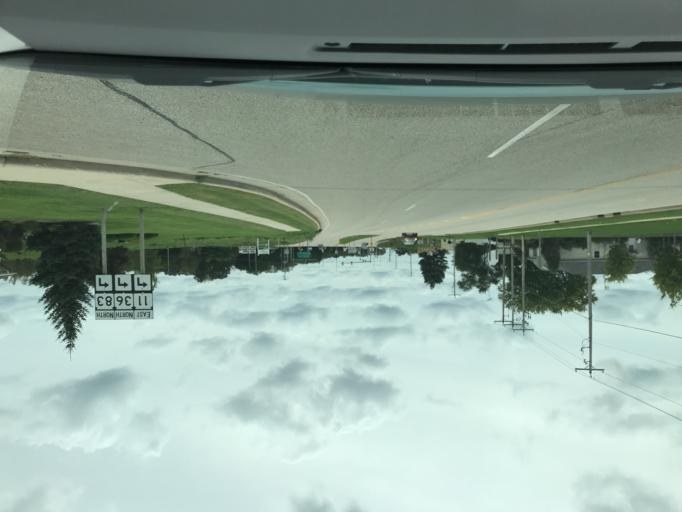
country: US
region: Wisconsin
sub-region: Racine County
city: Burlington
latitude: 42.6599
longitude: -88.2612
